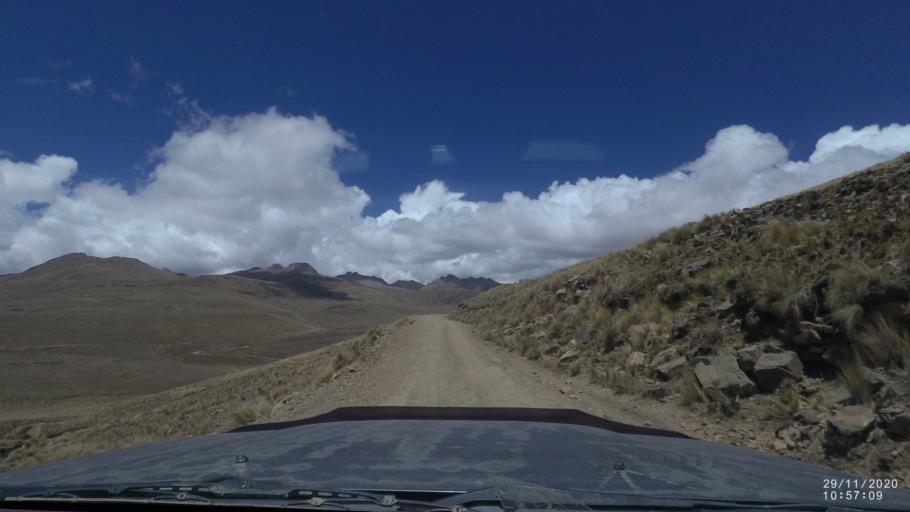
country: BO
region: Cochabamba
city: Cochabamba
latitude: -17.2152
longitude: -66.2265
